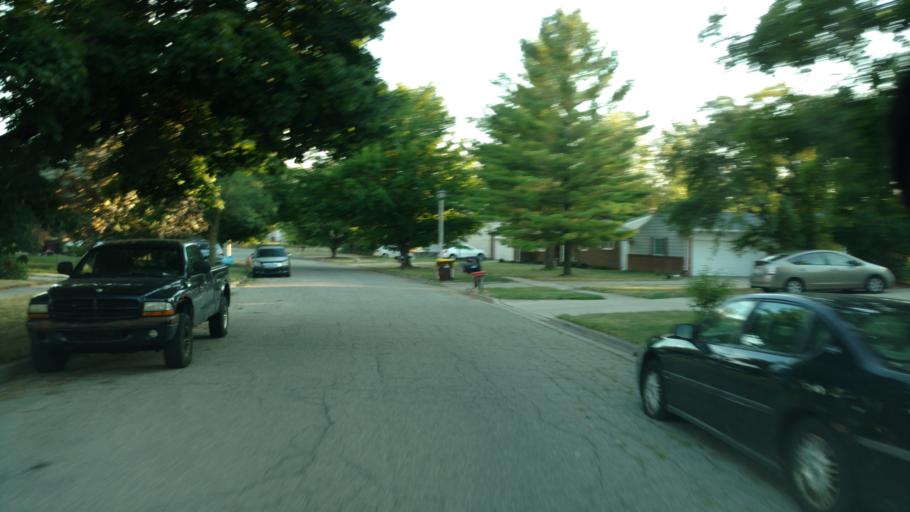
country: US
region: Michigan
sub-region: Eaton County
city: Waverly
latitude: 42.7217
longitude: -84.6291
